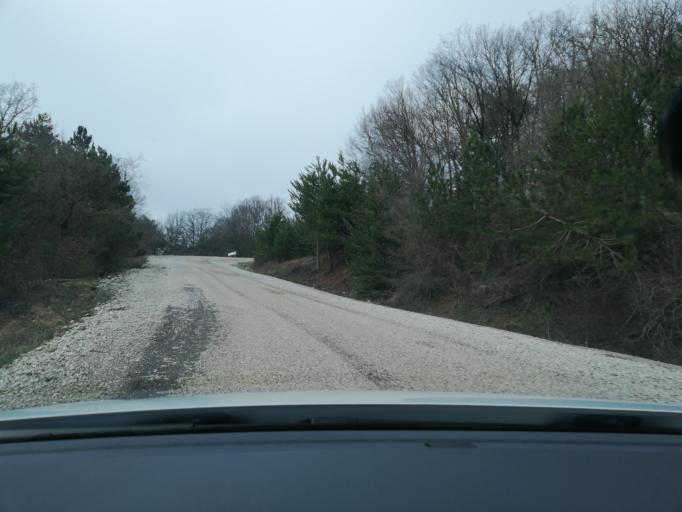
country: TR
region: Bolu
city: Bolu
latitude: 40.6603
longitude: 31.4695
